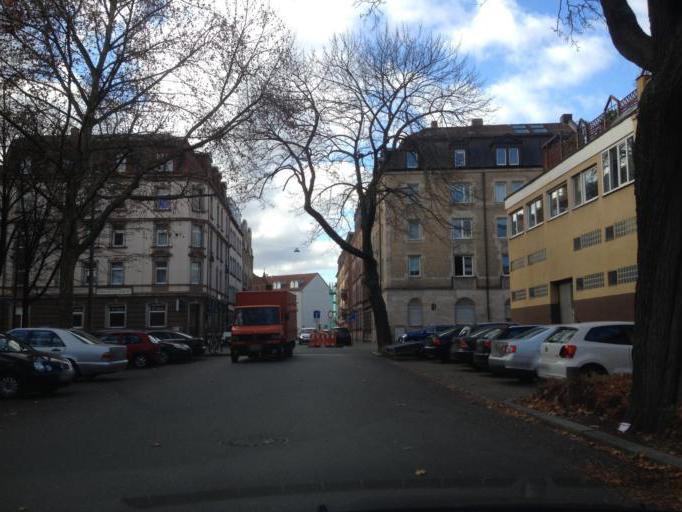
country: DE
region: Bavaria
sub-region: Regierungsbezirk Mittelfranken
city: Grossreuth bei Schweinau
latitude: 49.4351
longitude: 11.0515
